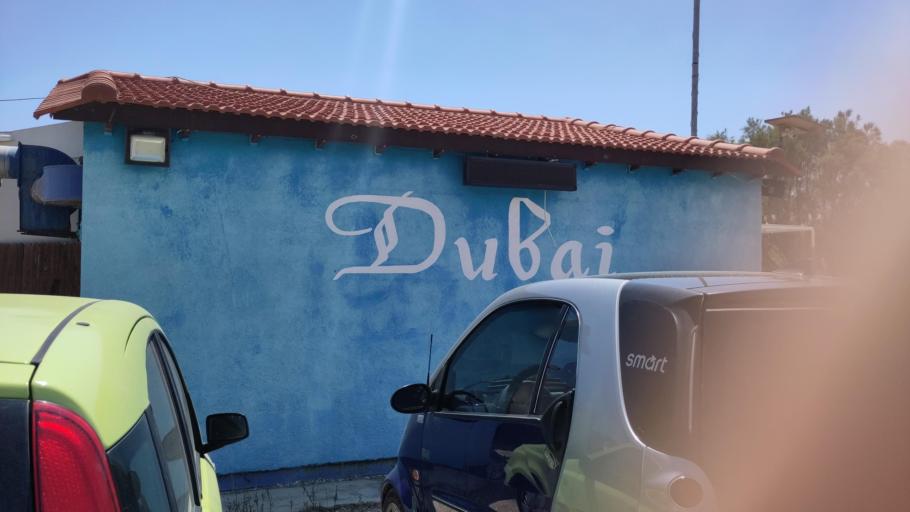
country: GR
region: South Aegean
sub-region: Nomos Dodekanisou
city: Afantou
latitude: 36.2498
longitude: 28.1687
